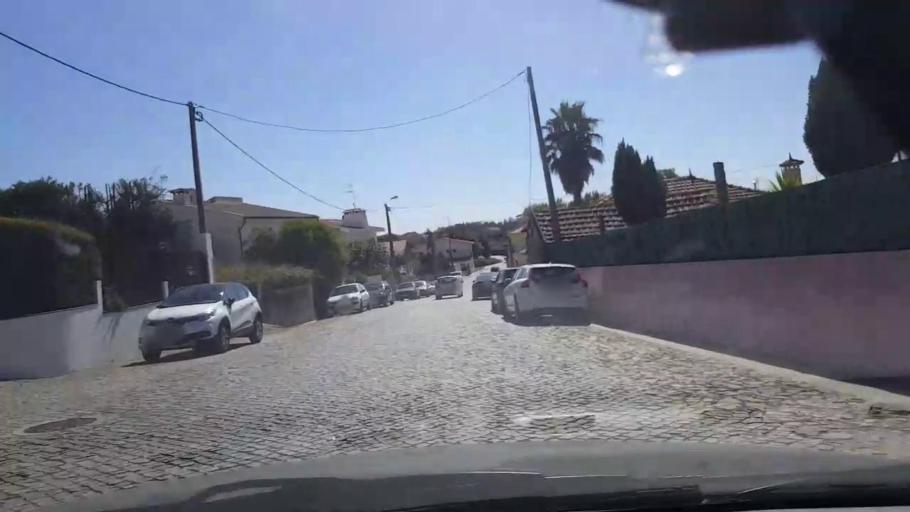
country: PT
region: Porto
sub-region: Vila do Conde
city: Arvore
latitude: 41.3203
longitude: -8.7237
